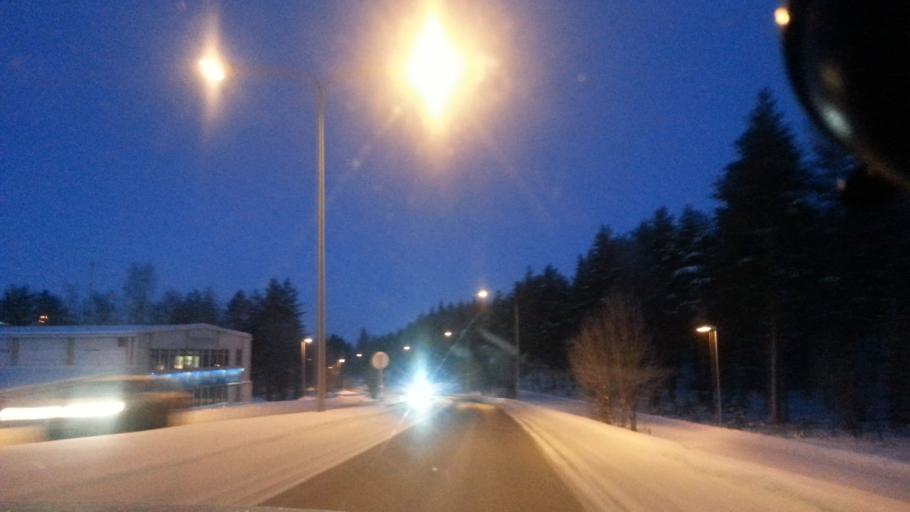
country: FI
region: Lapland
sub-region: Rovaniemi
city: Rovaniemi
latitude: 66.4991
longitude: 25.7557
